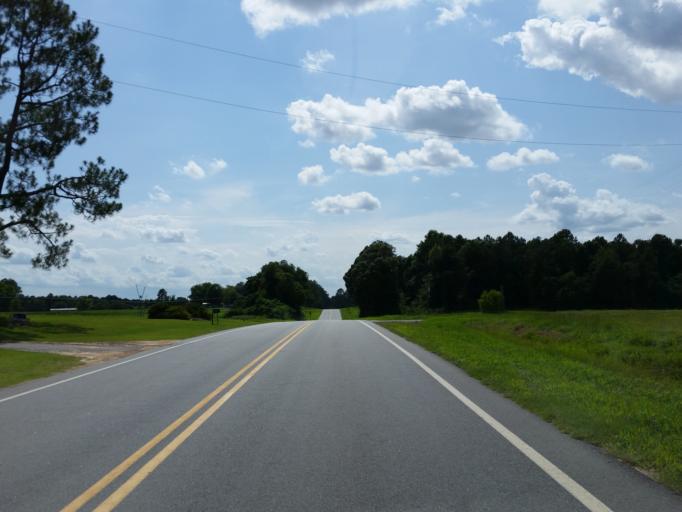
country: US
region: Georgia
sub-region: Turner County
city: Ashburn
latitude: 31.6589
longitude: -83.5846
